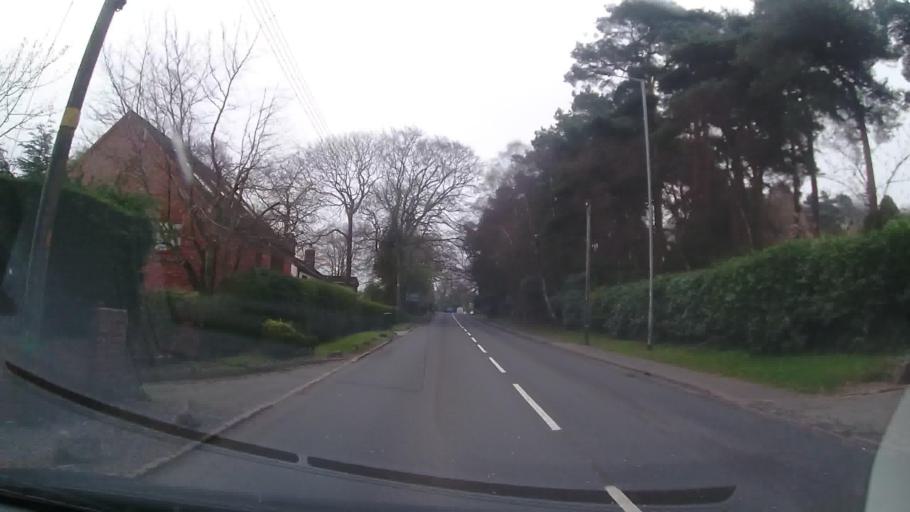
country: GB
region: England
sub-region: Staffordshire
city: Standon
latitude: 52.9226
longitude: -2.3851
